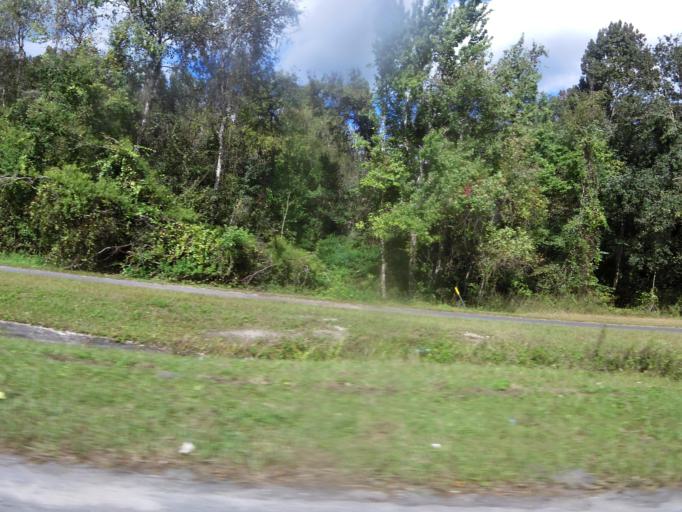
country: US
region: Florida
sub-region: Alachua County
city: Alachua
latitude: 29.7034
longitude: -82.3816
